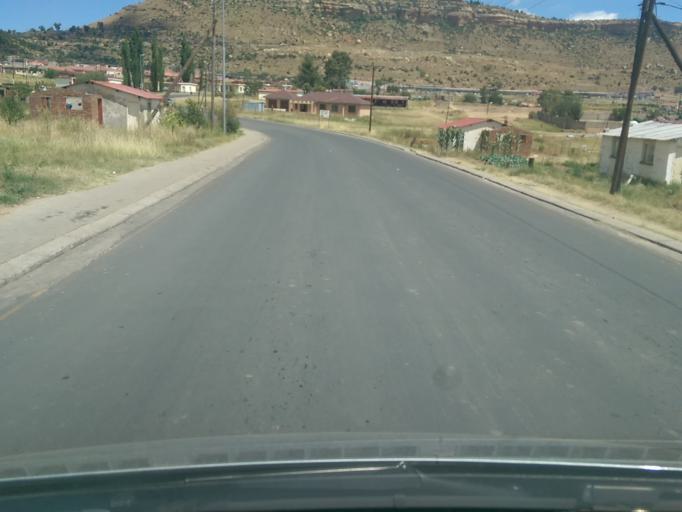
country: LS
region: Maseru
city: Maseru
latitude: -29.3265
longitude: 27.4864
